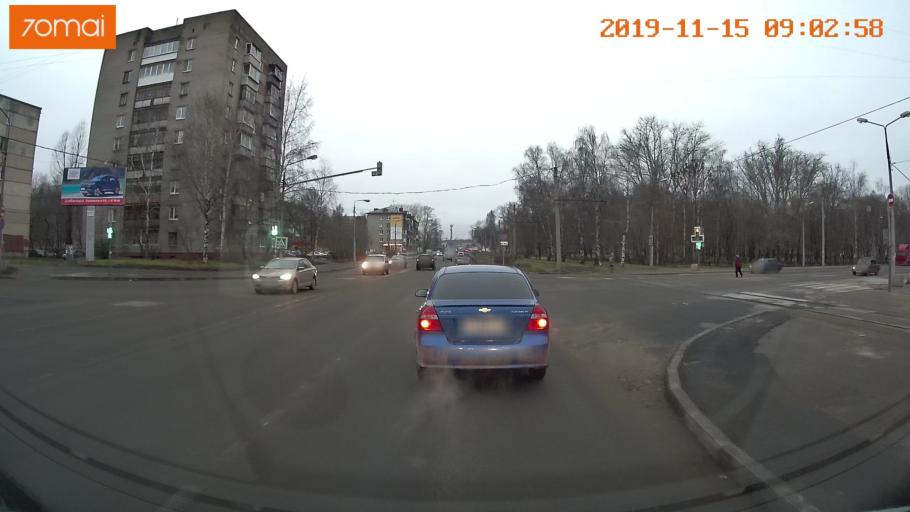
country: RU
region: Vologda
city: Cherepovets
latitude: 59.1371
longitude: 37.9255
